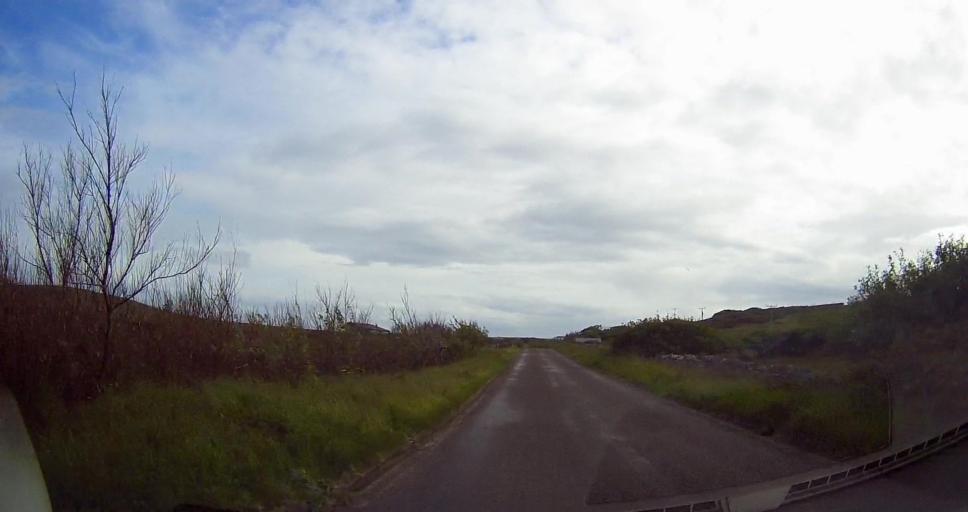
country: GB
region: Scotland
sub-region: Orkney Islands
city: Stromness
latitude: 58.7911
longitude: -3.2584
